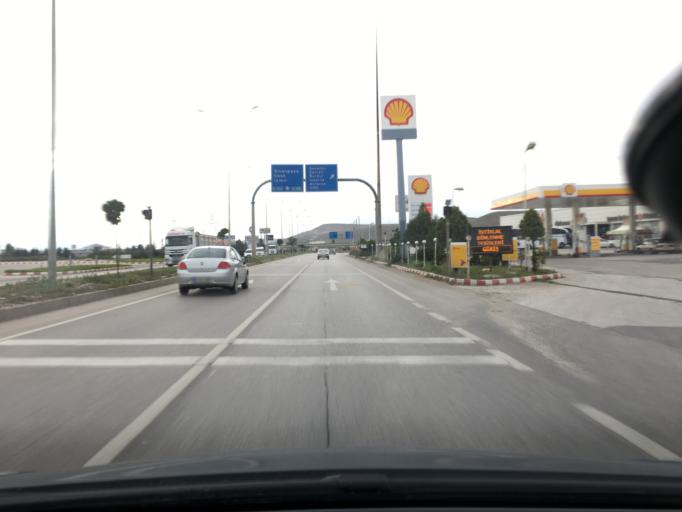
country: TR
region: Afyonkarahisar
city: Afyonkarahisar
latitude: 38.7956
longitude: 30.3953
